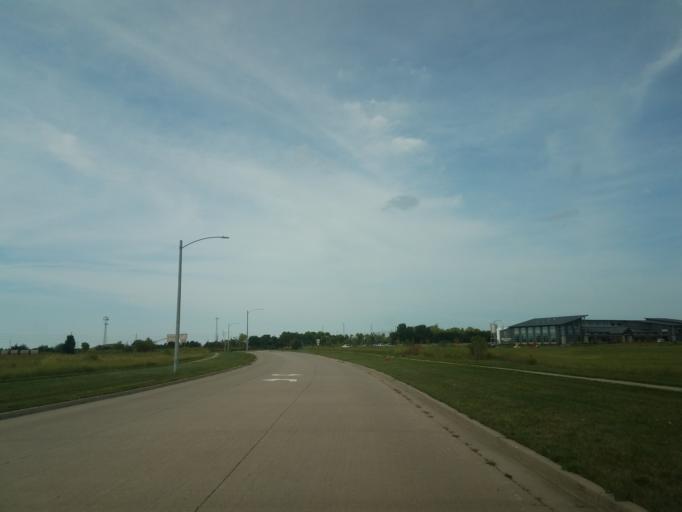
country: US
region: Illinois
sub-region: McLean County
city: Normal
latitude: 40.5273
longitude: -88.9492
